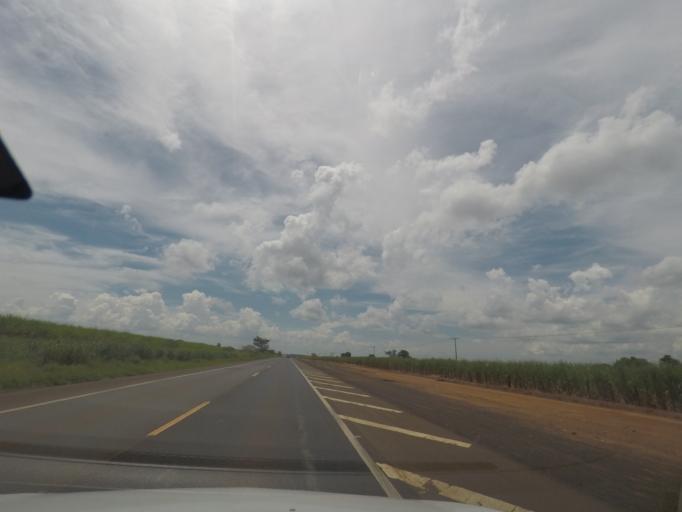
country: BR
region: Sao Paulo
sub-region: Barretos
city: Barretos
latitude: -20.3899
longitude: -48.6399
